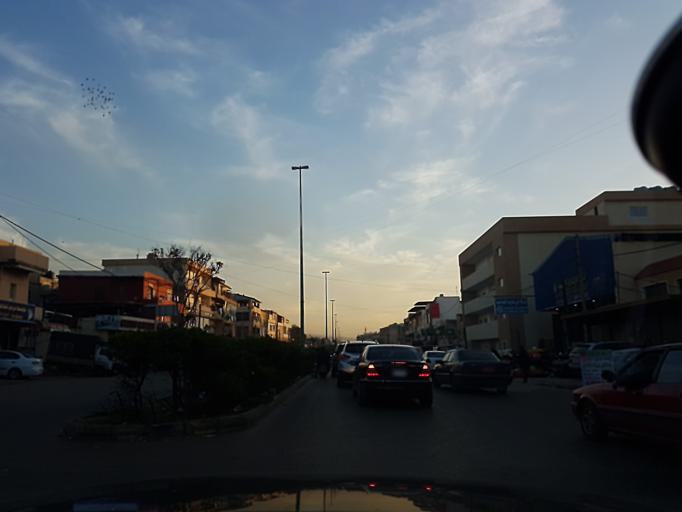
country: LB
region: Beyrouth
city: Beirut
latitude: 33.8405
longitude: 35.4848
